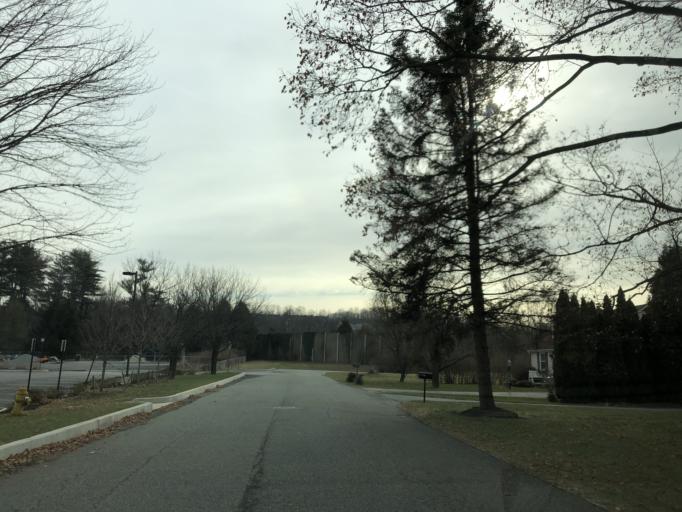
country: US
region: Pennsylvania
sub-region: Chester County
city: Exton
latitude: 40.0232
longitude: -75.6221
